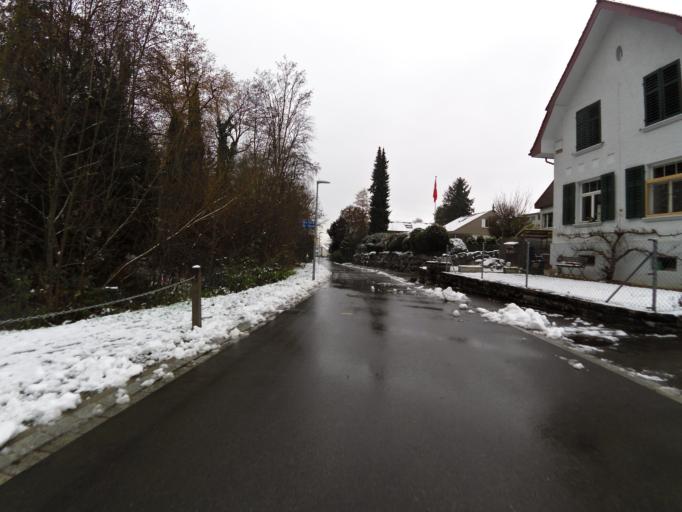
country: CH
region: Thurgau
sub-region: Frauenfeld District
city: Frauenfeld
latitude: 47.5585
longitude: 8.9076
